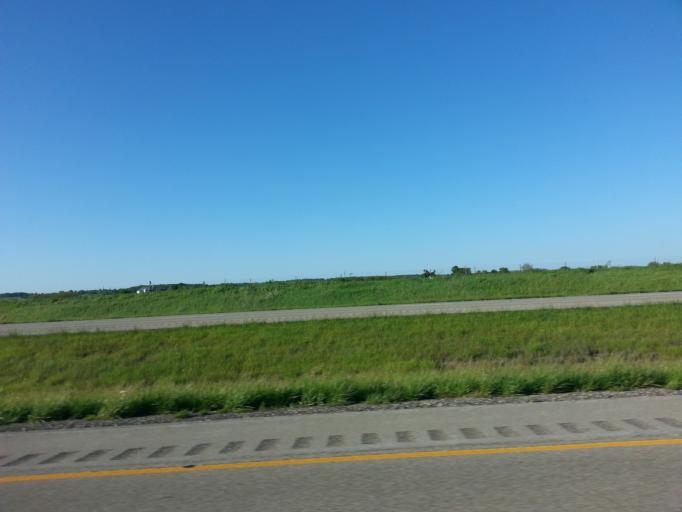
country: US
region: Illinois
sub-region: McLean County
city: Downs
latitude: 40.3775
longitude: -88.8485
